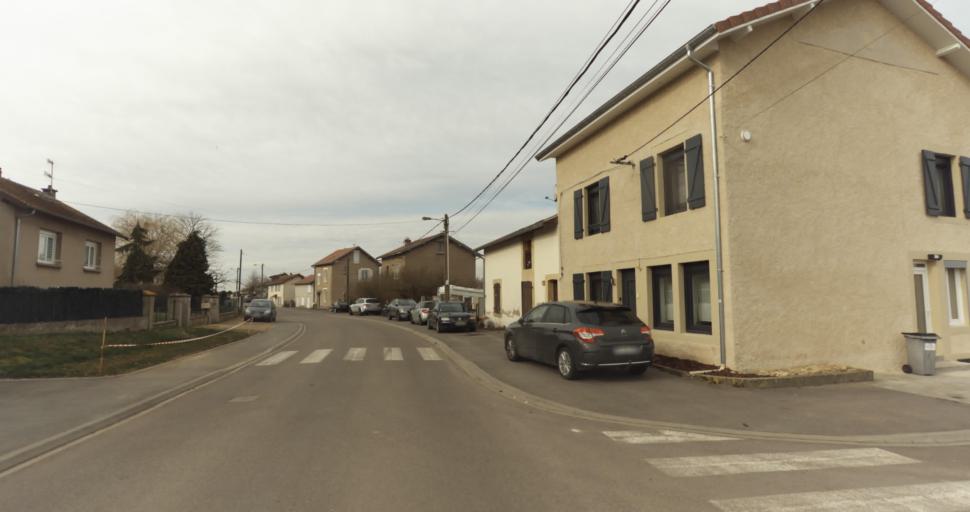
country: FR
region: Lorraine
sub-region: Departement de Meurthe-et-Moselle
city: Jarny
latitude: 49.1420
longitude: 5.8703
